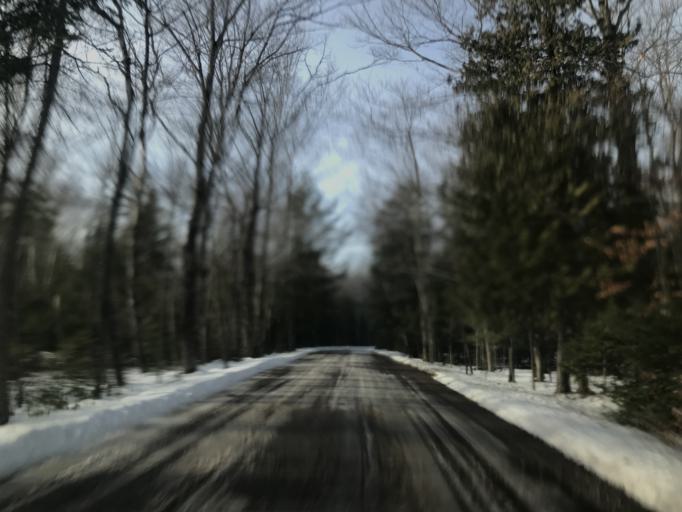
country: US
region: Wisconsin
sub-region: Door County
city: Sturgeon Bay
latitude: 45.1533
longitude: -87.0560
